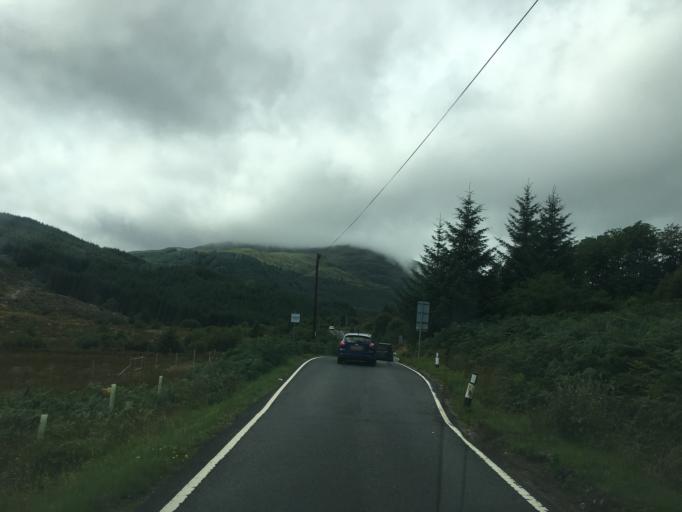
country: GB
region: Scotland
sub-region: Argyll and Bute
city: Dunoon
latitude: 55.9901
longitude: -5.0248
